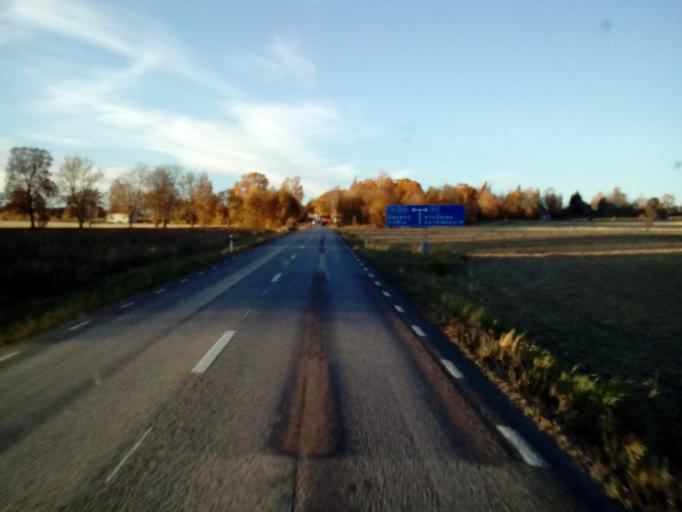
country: SE
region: OErebro
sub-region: Hallsbergs Kommun
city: Skollersta
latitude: 59.1263
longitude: 15.3265
